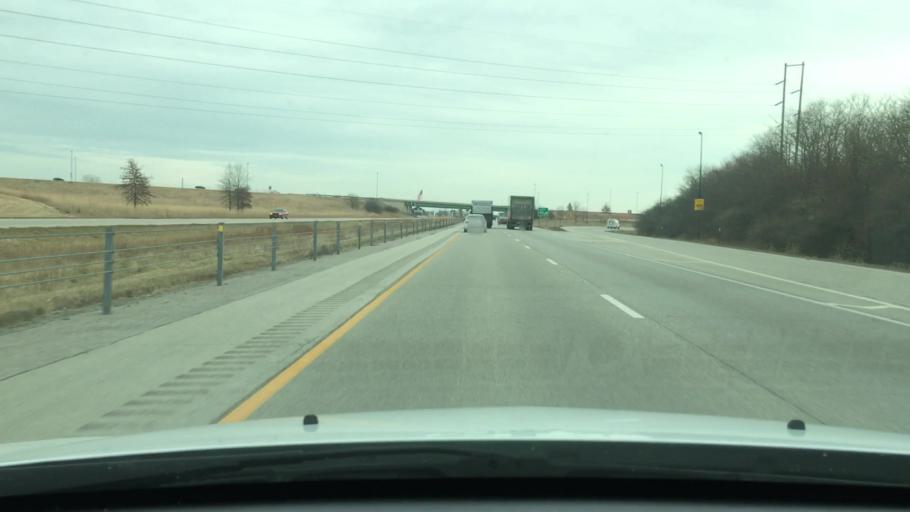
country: US
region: Illinois
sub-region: Sangamon County
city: Jerome
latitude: 39.7441
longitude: -89.7113
